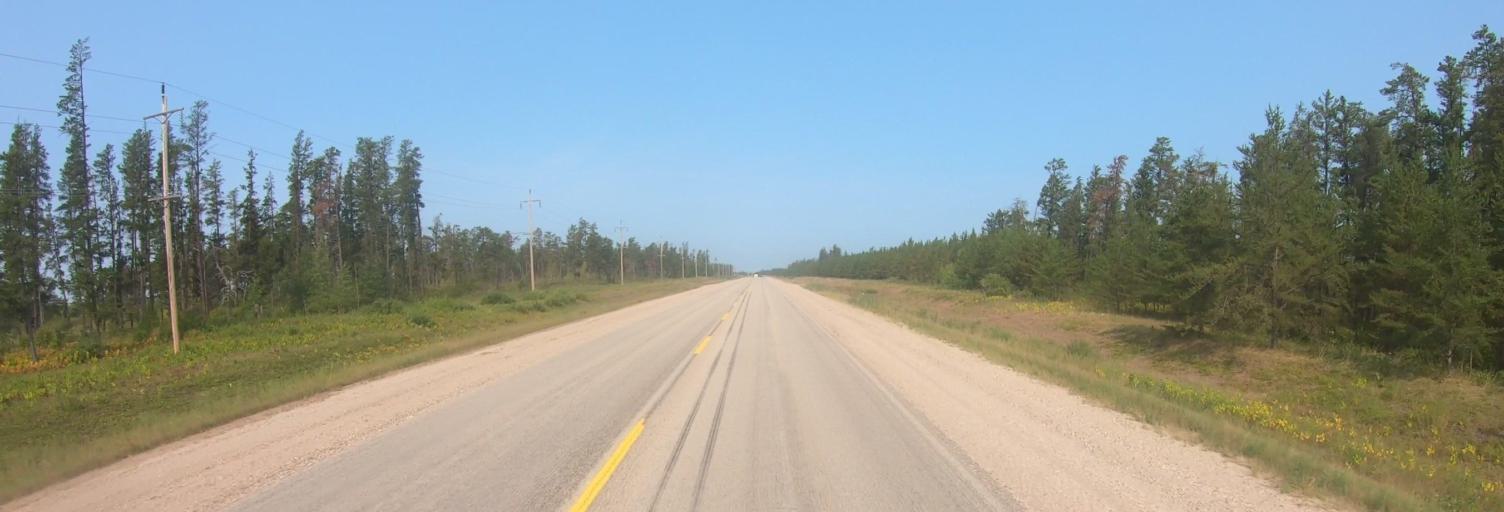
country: US
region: Minnesota
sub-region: Roseau County
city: Roseau
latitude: 49.0826
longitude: -95.8749
